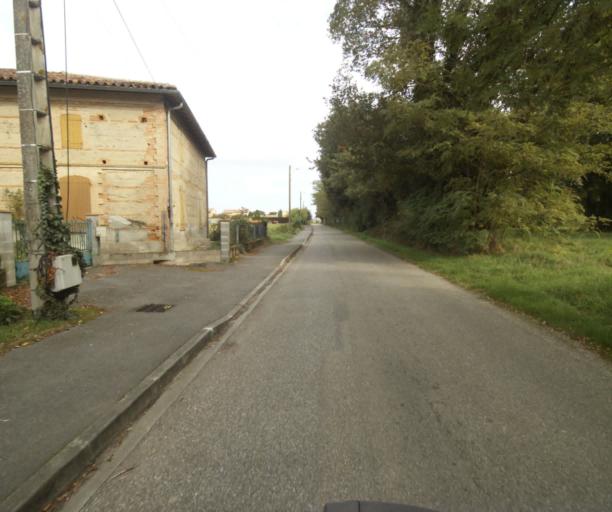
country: FR
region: Midi-Pyrenees
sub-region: Departement du Tarn-et-Garonne
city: Finhan
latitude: 43.9181
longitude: 1.2220
